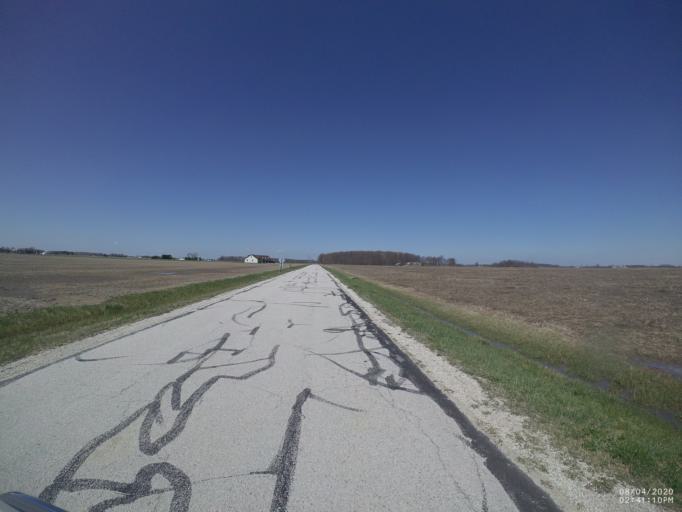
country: US
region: Ohio
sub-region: Sandusky County
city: Gibsonburg
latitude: 41.2841
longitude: -83.2969
